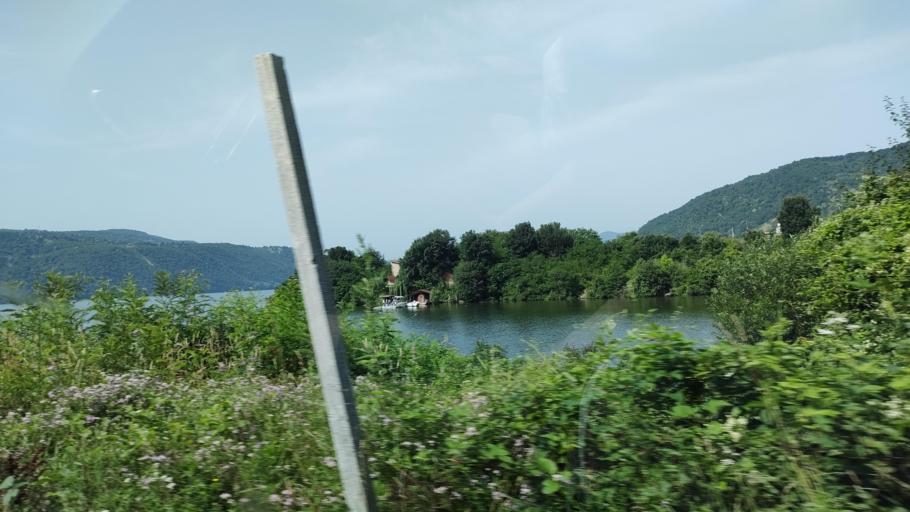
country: RO
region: Mehedinti
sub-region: Comuna Eselnita
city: Eselnita
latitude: 44.6838
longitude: 22.3471
